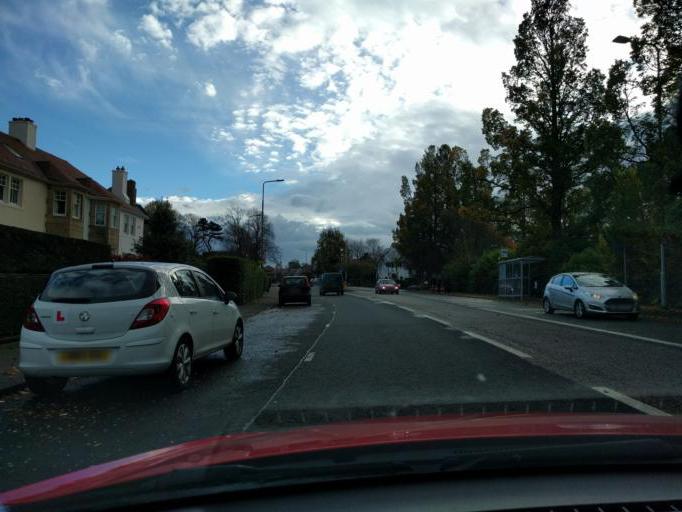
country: GB
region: Scotland
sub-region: Edinburgh
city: Edinburgh
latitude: 55.9132
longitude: -3.2137
